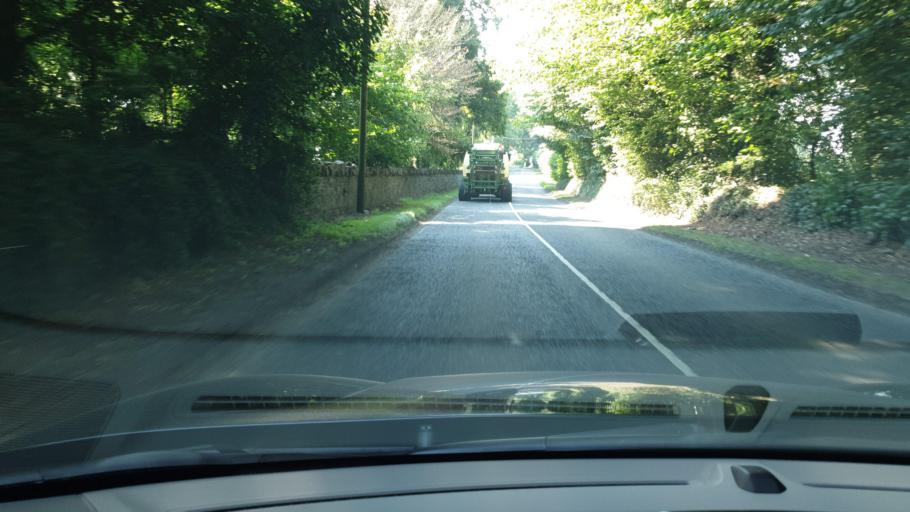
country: IE
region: Leinster
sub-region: An Mhi
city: Athboy
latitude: 53.5990
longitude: -6.8741
